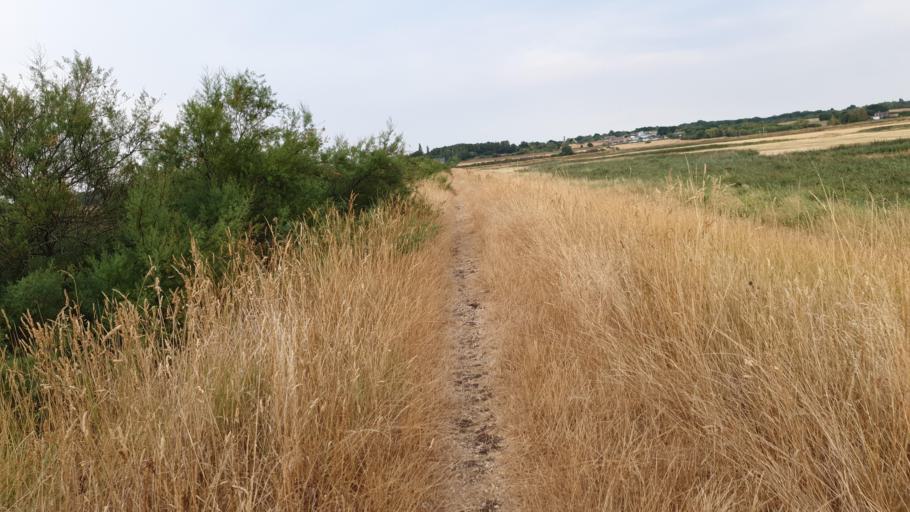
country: GB
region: England
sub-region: Essex
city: Alresford
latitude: 51.8322
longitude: 0.9869
